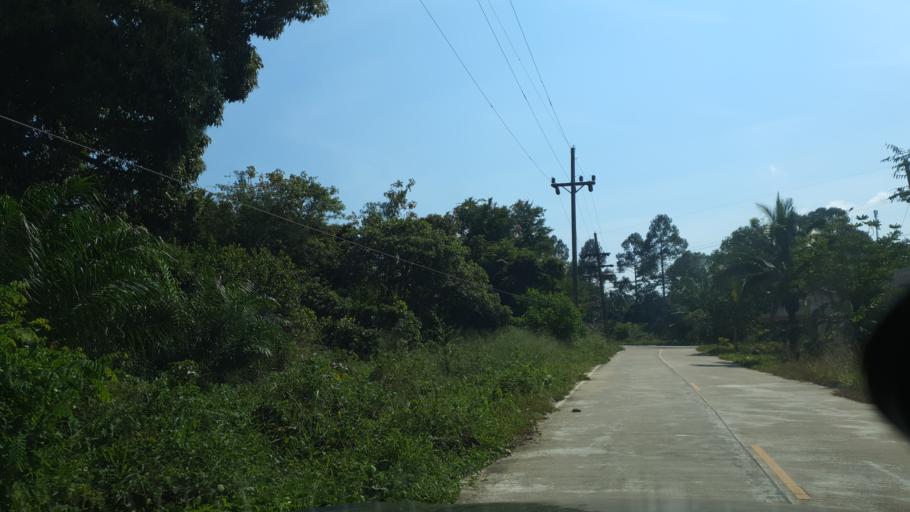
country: TH
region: Surat Thani
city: Tha Chana
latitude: 9.5894
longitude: 99.2014
